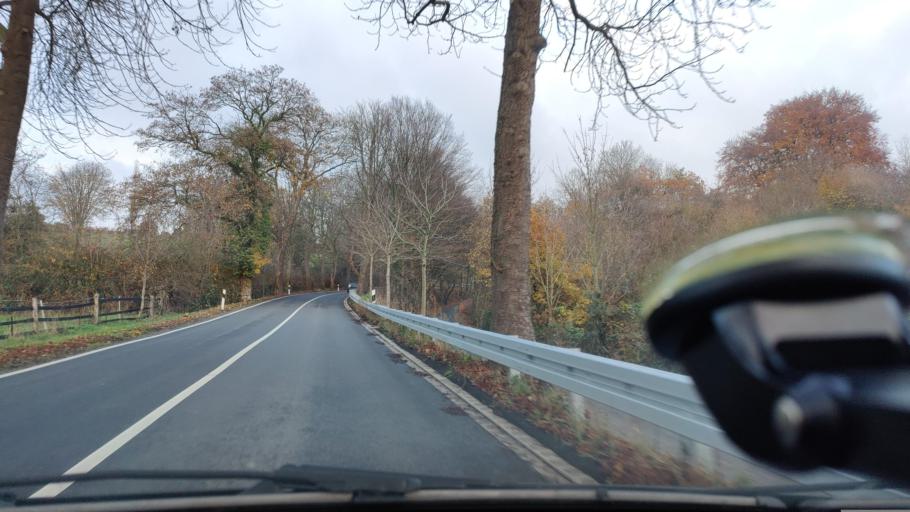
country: DE
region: North Rhine-Westphalia
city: Lunen
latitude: 51.6508
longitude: 7.5349
